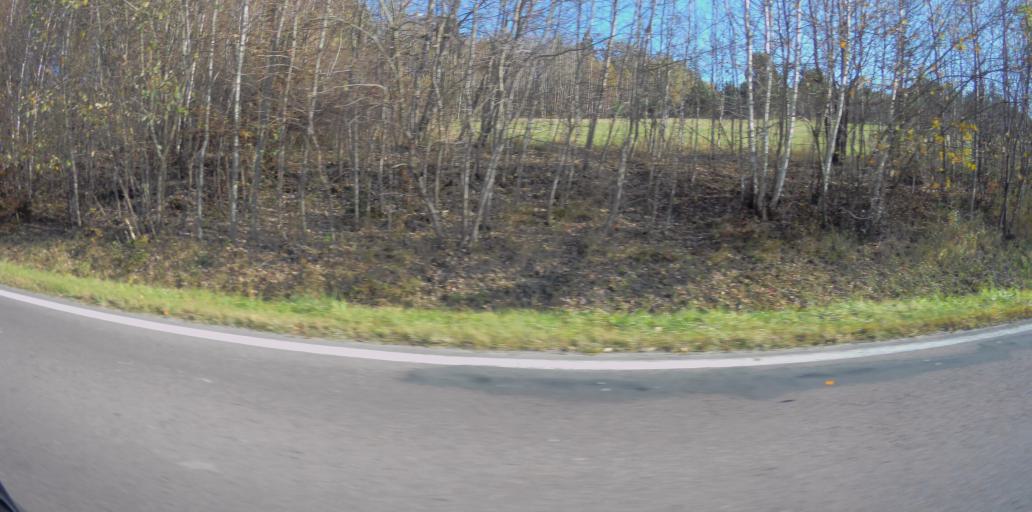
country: PL
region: Subcarpathian Voivodeship
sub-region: Powiat bieszczadzki
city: Ustrzyki Dolne
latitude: 49.5345
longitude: 22.5977
